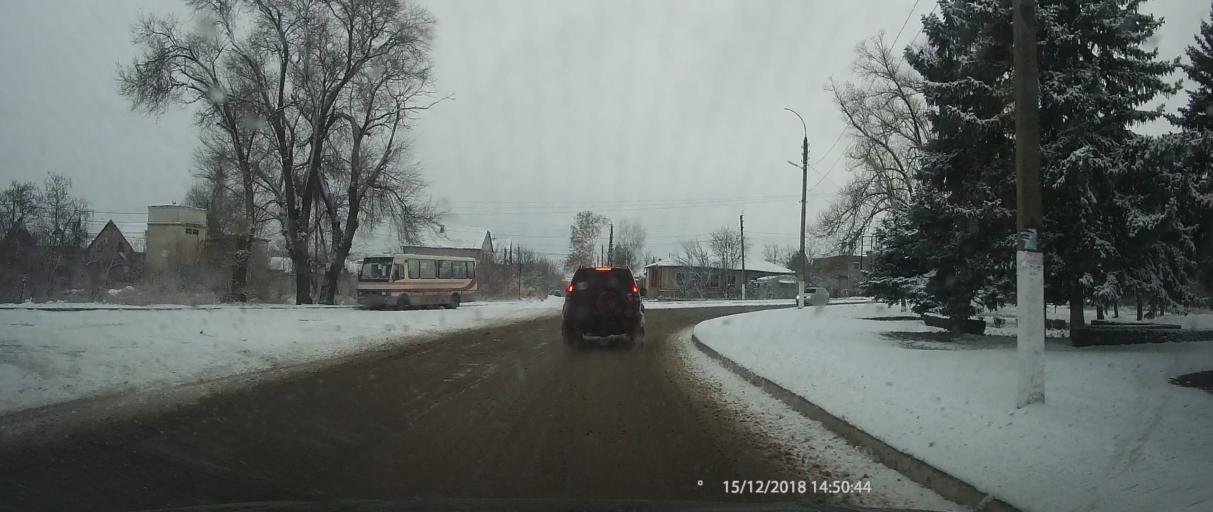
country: MD
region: Cahul
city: Cahul
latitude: 45.9000
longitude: 28.1862
